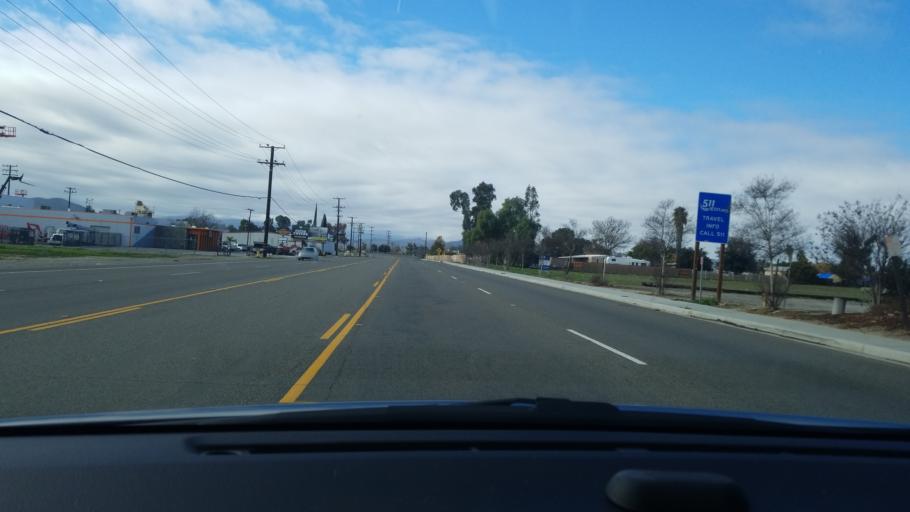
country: US
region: California
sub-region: Riverside County
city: Romoland
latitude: 33.7430
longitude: -117.1654
